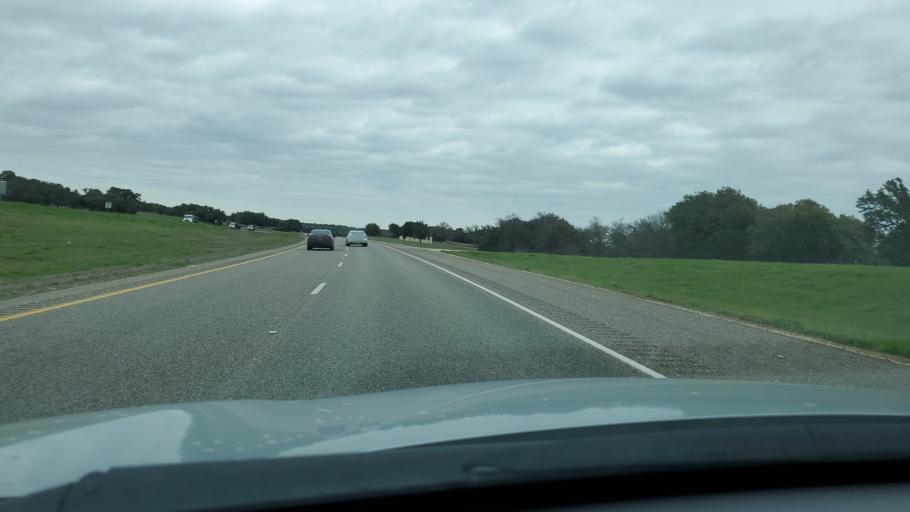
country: US
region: Texas
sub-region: Williamson County
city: Florence
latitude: 30.8994
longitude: -97.8003
